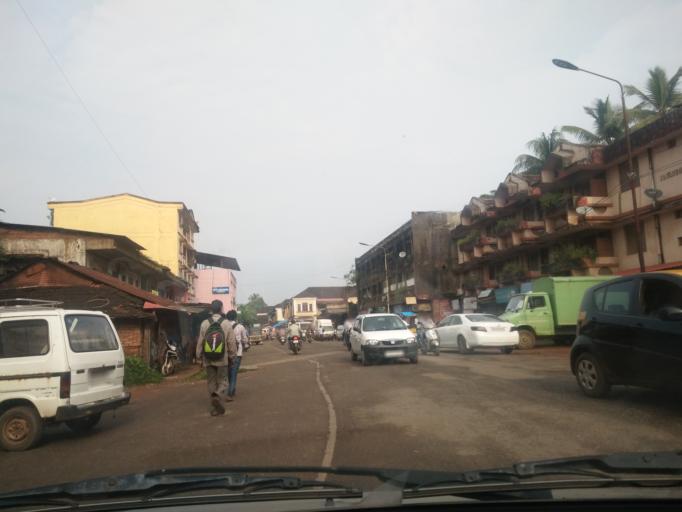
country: IN
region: Goa
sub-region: South Goa
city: Madgaon
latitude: 15.2685
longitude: 73.9595
